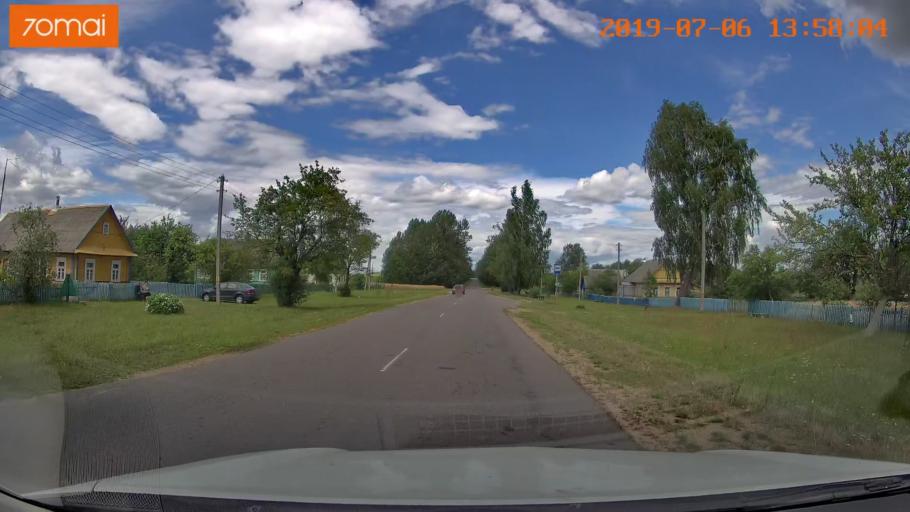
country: BY
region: Minsk
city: Ivyanyets
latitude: 53.7801
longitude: 26.8079
